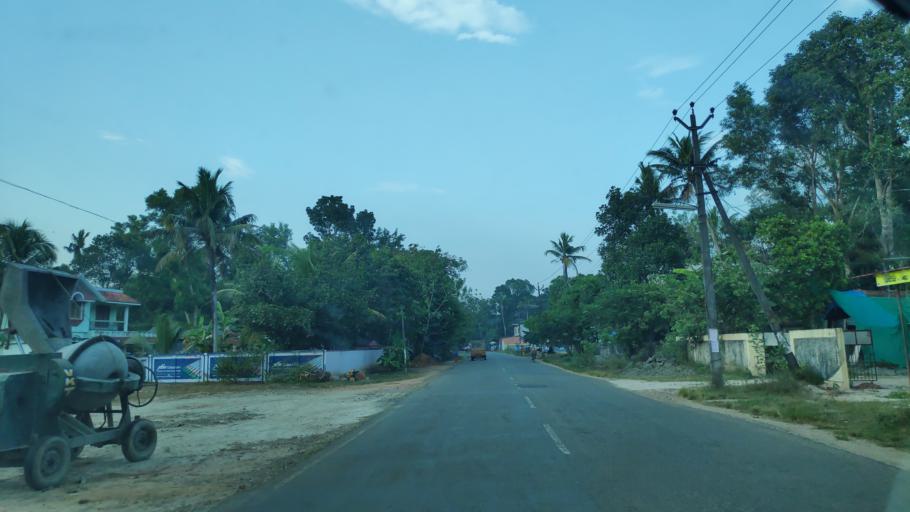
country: IN
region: Kerala
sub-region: Alappuzha
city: Shertallai
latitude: 9.6378
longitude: 76.3717
